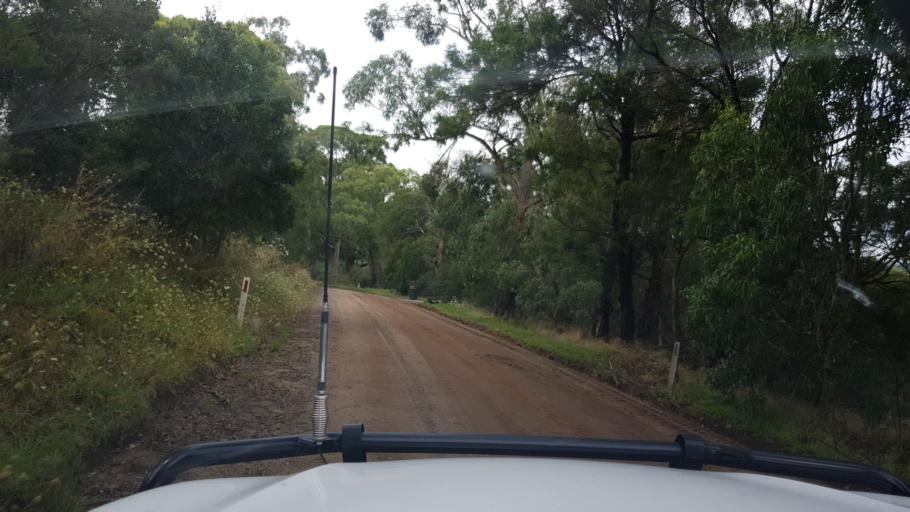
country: AU
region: Victoria
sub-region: Latrobe
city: Moe
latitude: -38.0731
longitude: 146.1452
